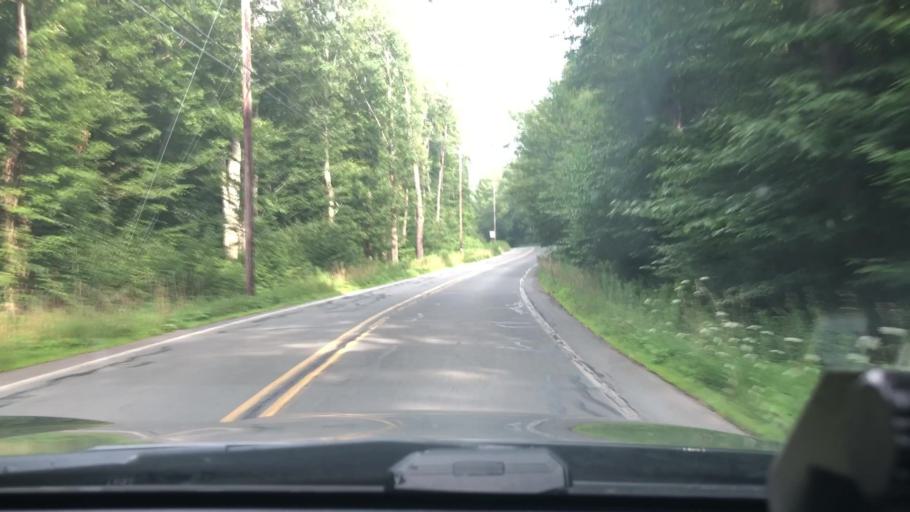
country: US
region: Pennsylvania
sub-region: Lackawanna County
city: Moscow
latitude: 41.2479
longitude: -75.4903
